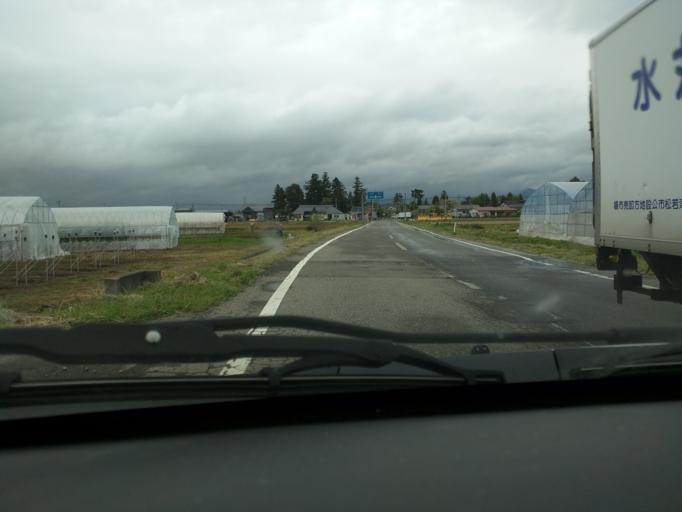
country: JP
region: Fukushima
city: Kitakata
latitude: 37.6051
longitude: 139.8731
